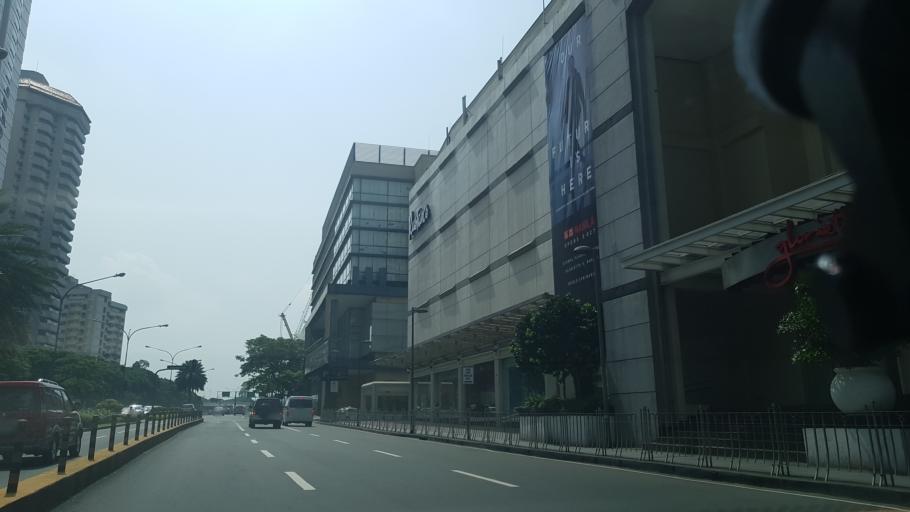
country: PH
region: Metro Manila
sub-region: Makati City
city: Makati City
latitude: 14.5529
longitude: 121.0268
